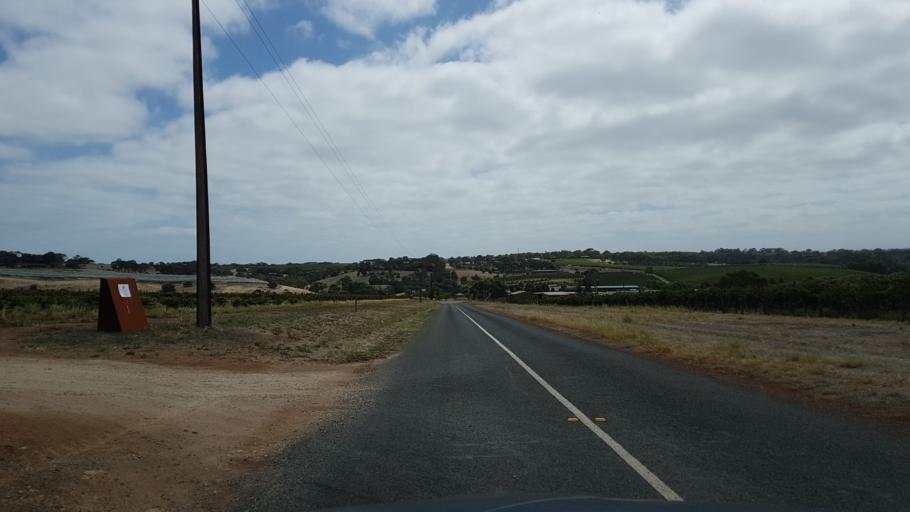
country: AU
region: South Australia
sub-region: Onkaparinga
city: McLaren Vale
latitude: -35.2130
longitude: 138.5175
